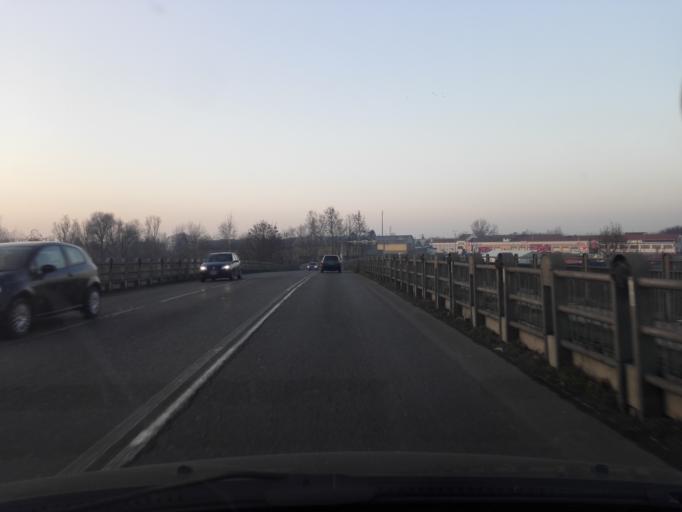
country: IT
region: Piedmont
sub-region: Provincia di Alessandria
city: Alessandria
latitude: 44.9150
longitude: 8.6016
